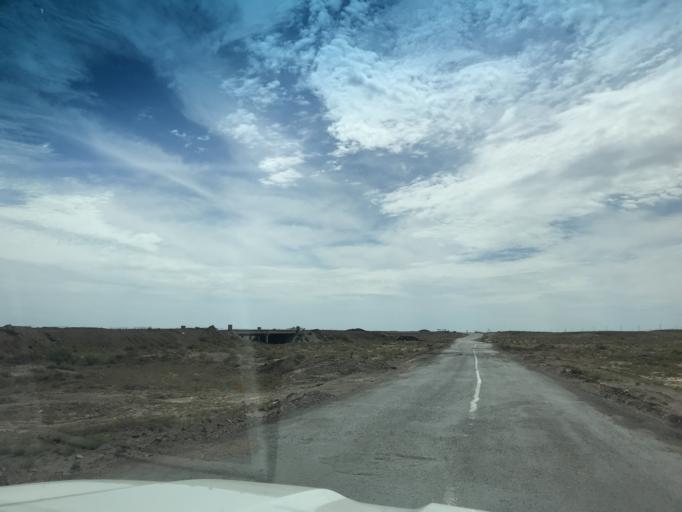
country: KZ
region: Almaty Oblysy
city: Ulken
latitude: 45.2443
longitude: 73.8204
